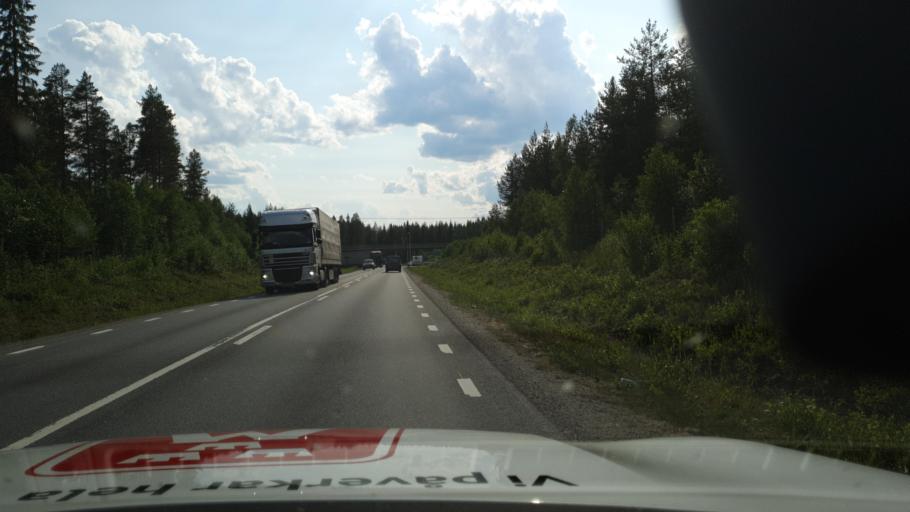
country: SE
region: Vaesterbotten
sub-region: Skelleftea Kommun
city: Burea
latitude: 64.6485
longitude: 21.1442
